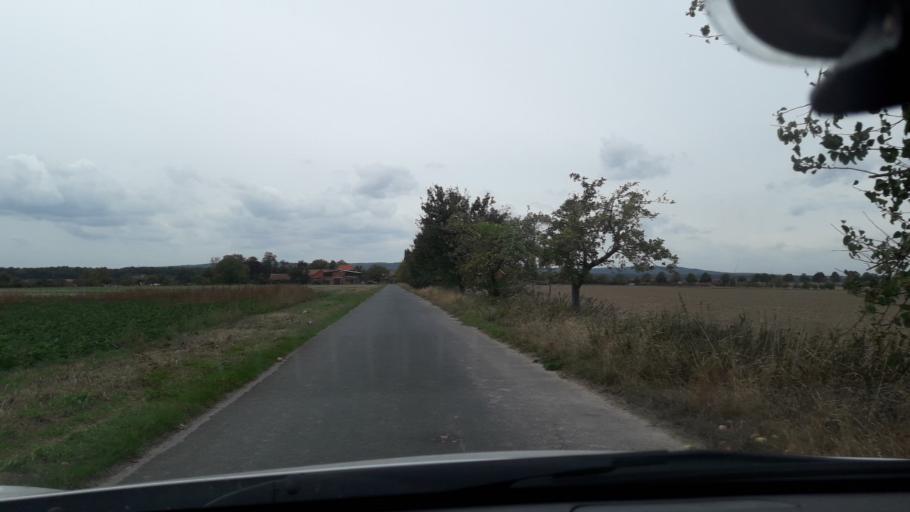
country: DE
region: Lower Saxony
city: Flothe
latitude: 52.0882
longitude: 10.4812
